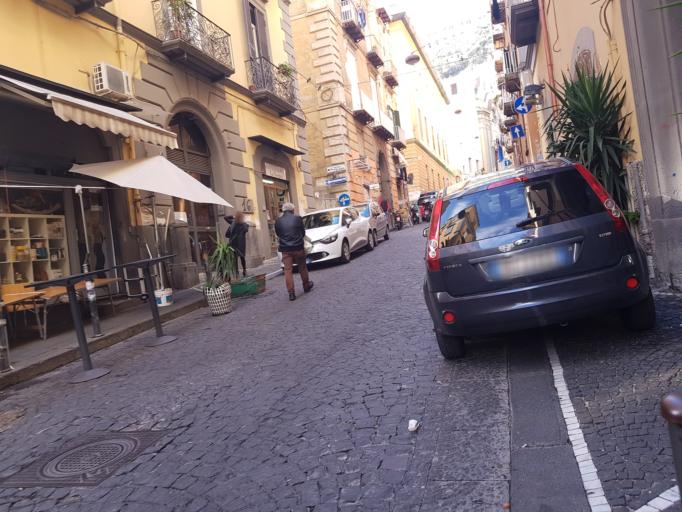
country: IT
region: Campania
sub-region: Provincia di Napoli
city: Napoli
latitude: 40.8429
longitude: 14.2474
